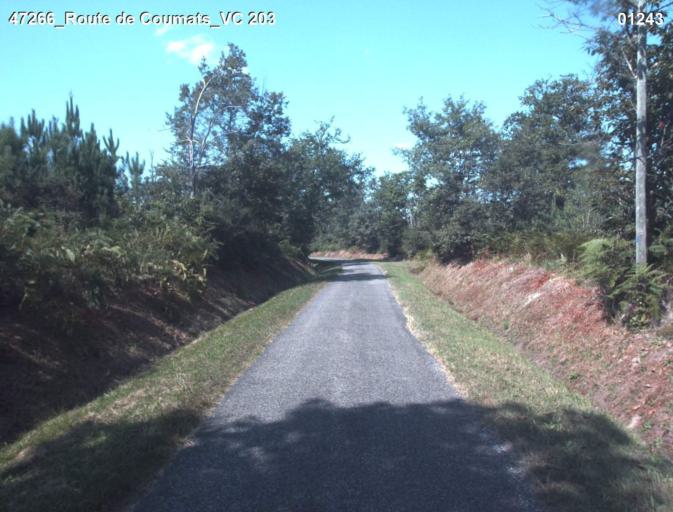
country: FR
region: Aquitaine
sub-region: Departement des Landes
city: Gabarret
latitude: 44.0069
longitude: 0.0923
